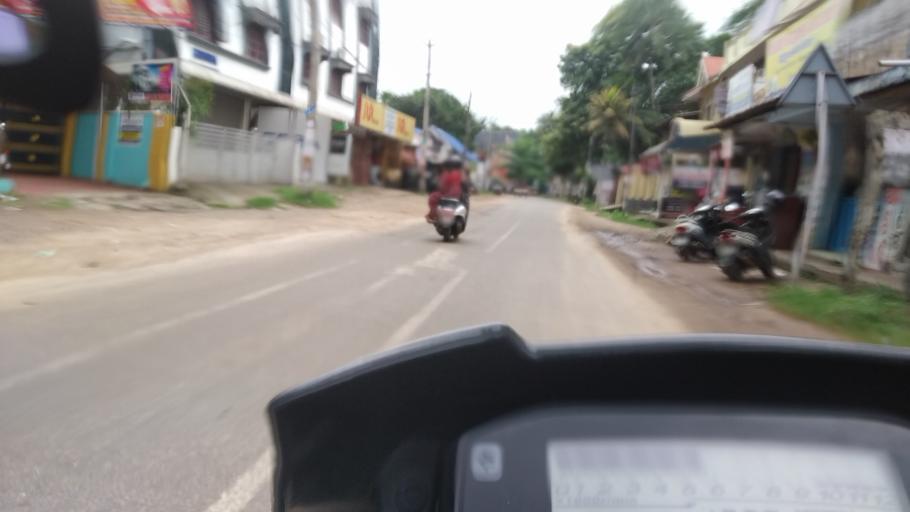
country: IN
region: Kerala
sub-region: Thiruvananthapuram
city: Attingal
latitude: 8.6941
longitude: 76.8113
